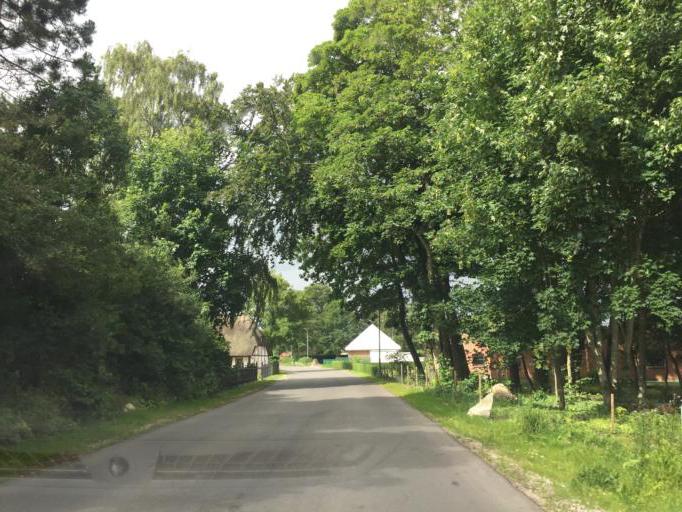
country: DK
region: South Denmark
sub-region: Faaborg-Midtfyn Kommune
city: Arslev
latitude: 55.2971
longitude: 10.4573
